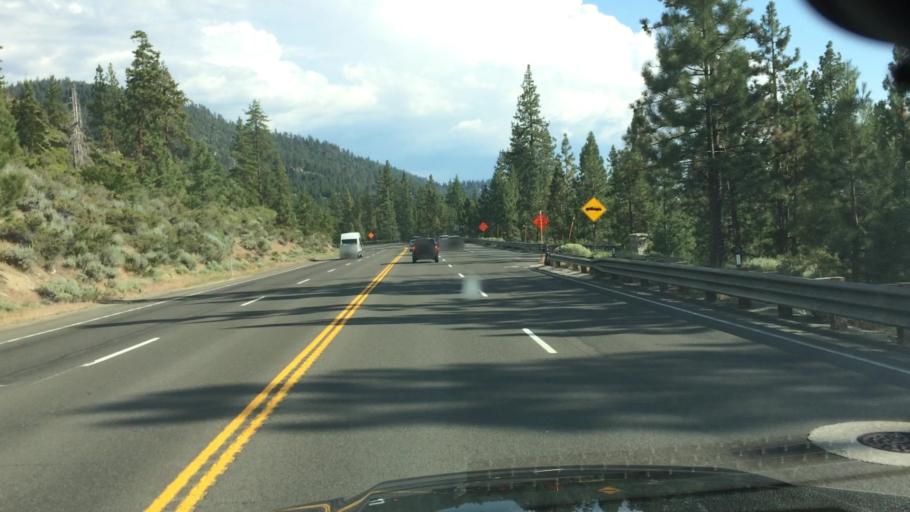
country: US
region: Nevada
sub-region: Douglas County
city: Kingsbury
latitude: 39.0792
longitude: -119.9427
